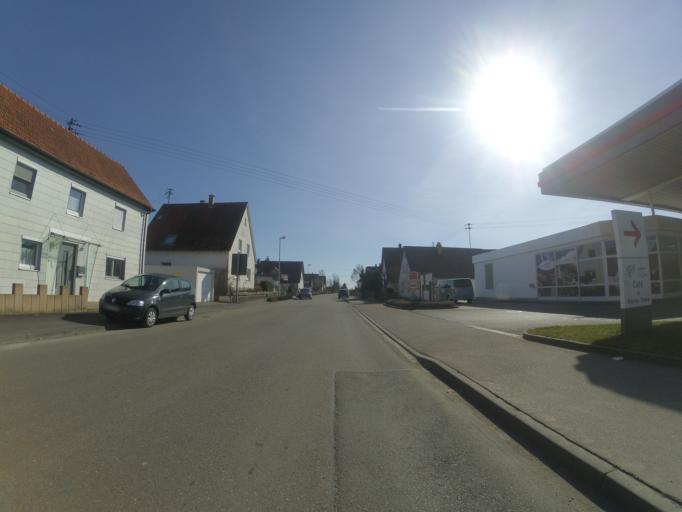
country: DE
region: Baden-Wuerttemberg
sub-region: Regierungsbezirk Stuttgart
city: Niederstotzingen
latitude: 48.5362
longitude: 10.2372
